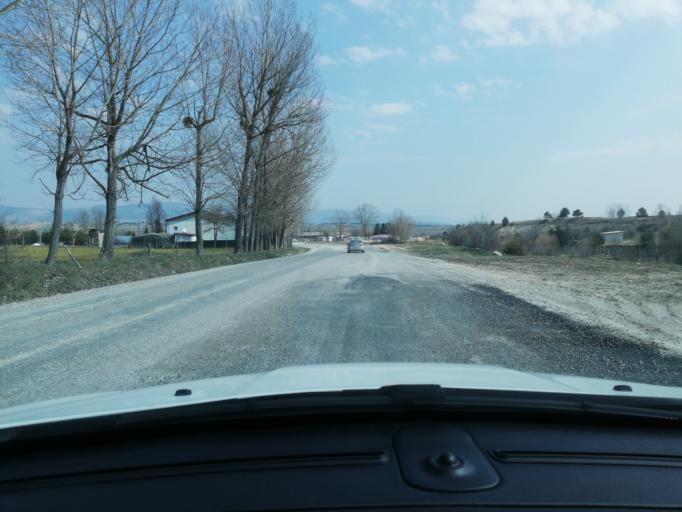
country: TR
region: Kastamonu
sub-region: Cide
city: Kastamonu
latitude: 41.4456
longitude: 33.7614
